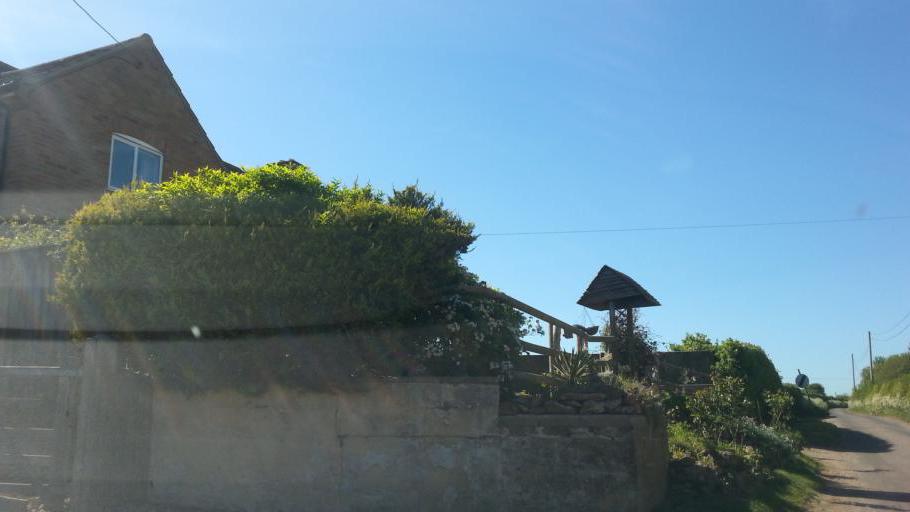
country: GB
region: England
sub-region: Somerset
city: Milborne Port
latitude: 50.9708
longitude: -2.4736
